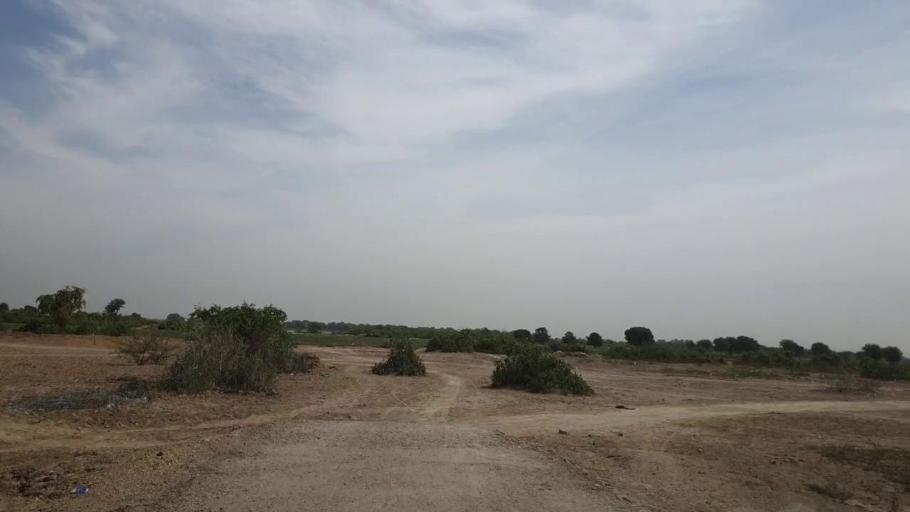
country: PK
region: Sindh
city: Kunri
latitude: 25.2078
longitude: 69.5886
